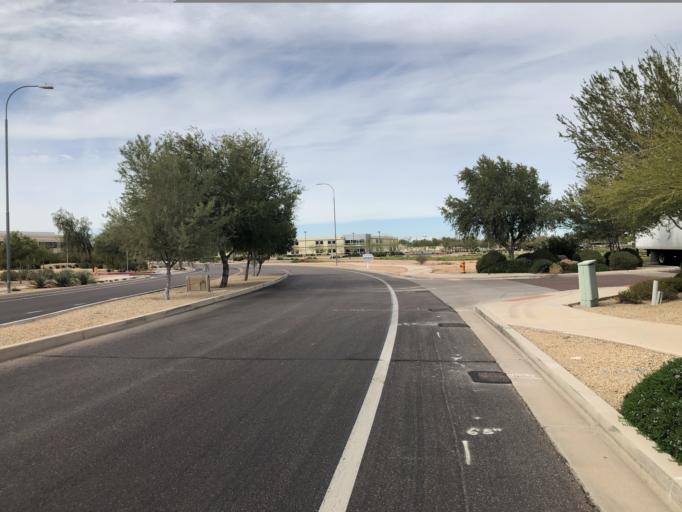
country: US
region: Arizona
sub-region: Maricopa County
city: Chandler
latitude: 33.3095
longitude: -111.9136
